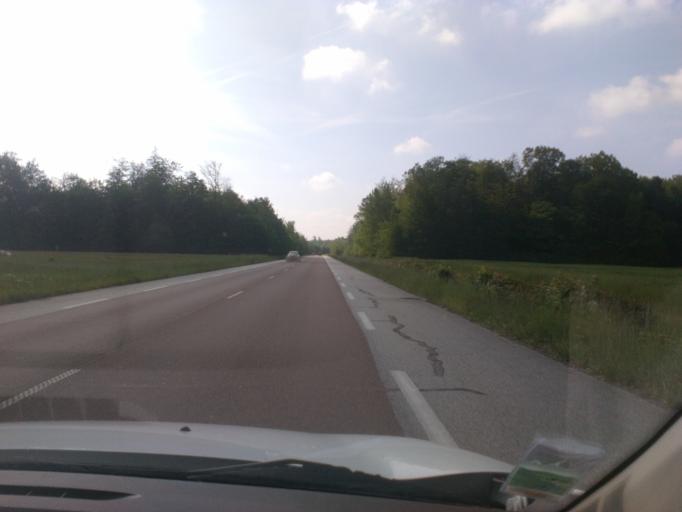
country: FR
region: Lorraine
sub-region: Departement des Vosges
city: Les Forges
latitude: 48.2003
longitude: 6.3942
